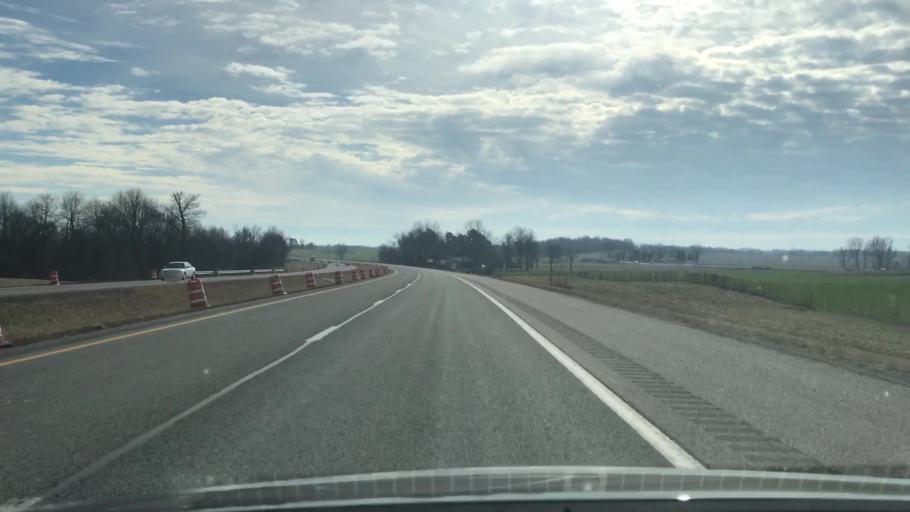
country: US
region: Kentucky
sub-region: Daviess County
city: Masonville
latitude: 37.6730
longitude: -87.0266
